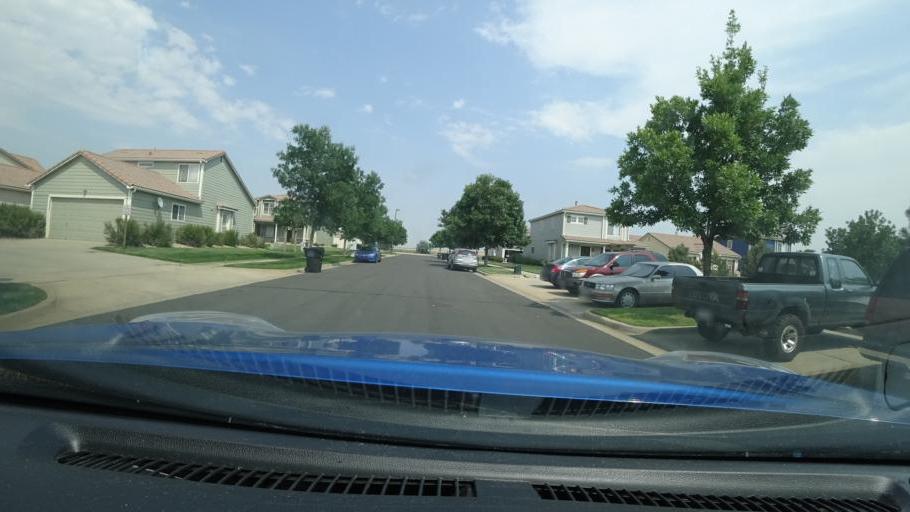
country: US
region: Colorado
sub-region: Adams County
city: Aurora
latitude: 39.7790
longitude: -104.7368
